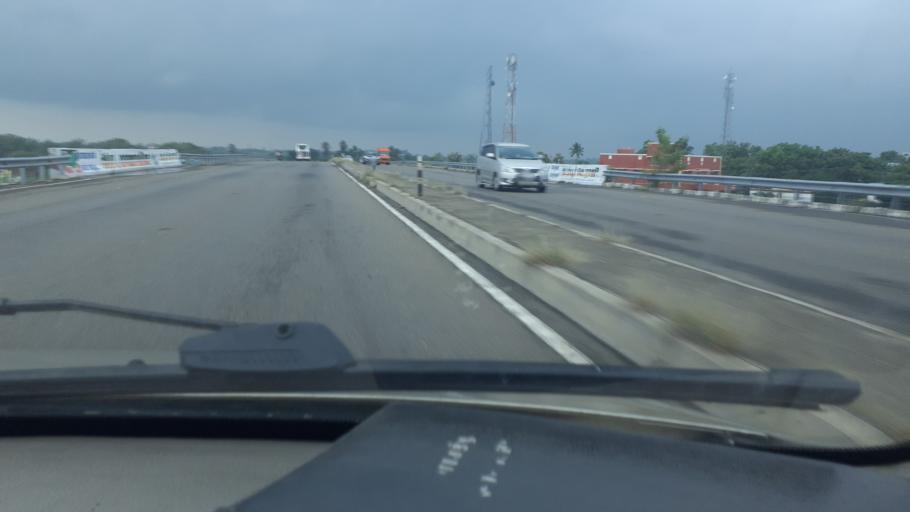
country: IN
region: Tamil Nadu
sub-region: Thoothukkudi
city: Kovilpatti
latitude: 9.1377
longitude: 77.8271
